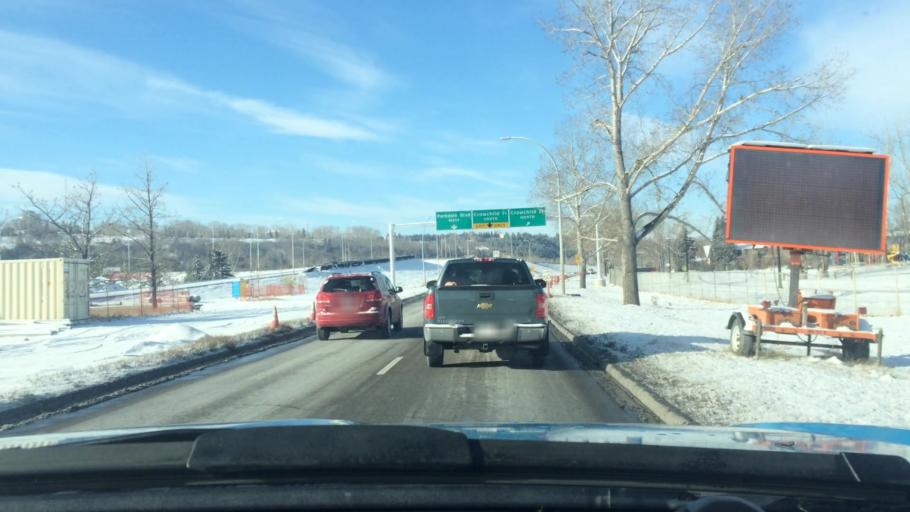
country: CA
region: Alberta
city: Calgary
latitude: 51.0494
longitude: -114.1118
